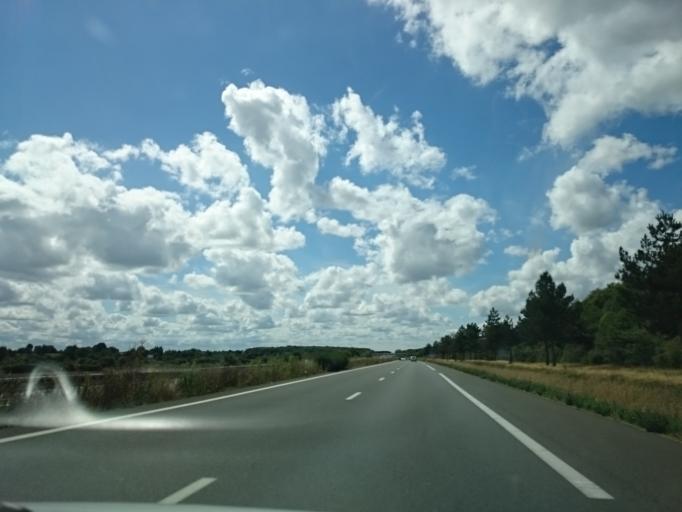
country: FR
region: Pays de la Loire
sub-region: Departement de Maine-et-Loire
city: Saint-Georges-sur-Loire
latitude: 47.4419
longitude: -0.7487
